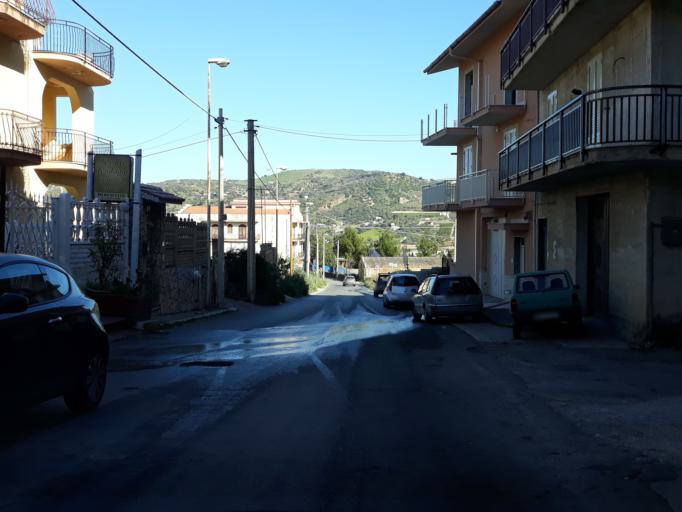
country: IT
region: Sicily
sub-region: Palermo
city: Misilmeri
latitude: 38.0278
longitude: 13.4524
